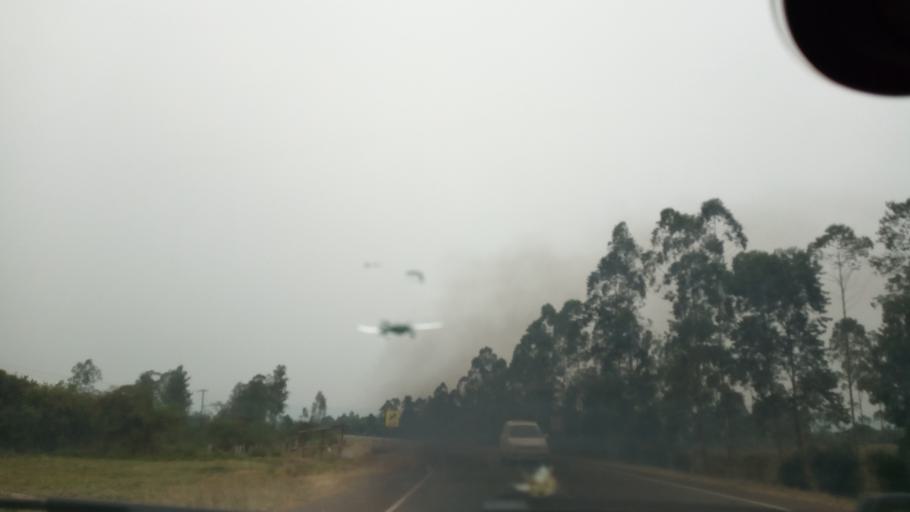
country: UG
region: Western Region
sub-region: Mbarara District
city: Mbarara
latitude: -0.7293
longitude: 30.7341
